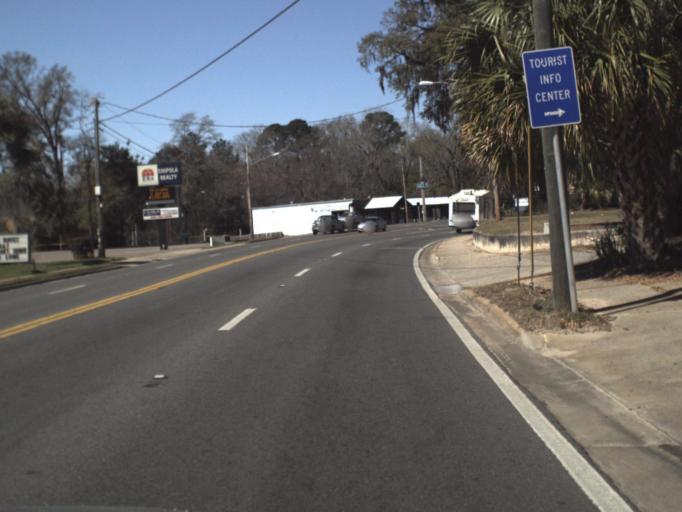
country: US
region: Florida
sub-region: Jackson County
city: Marianna
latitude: 30.7762
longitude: -85.2345
